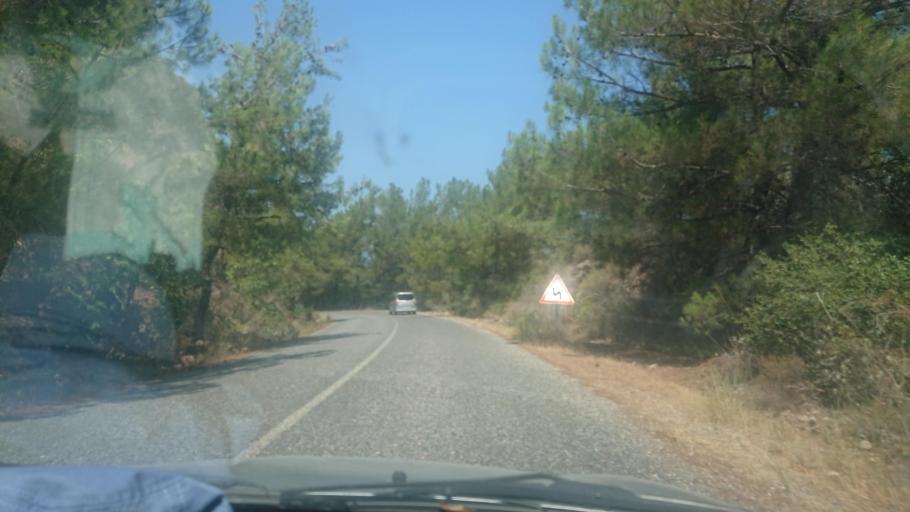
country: TR
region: Aydin
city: Atburgazi
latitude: 37.6973
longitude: 27.1747
